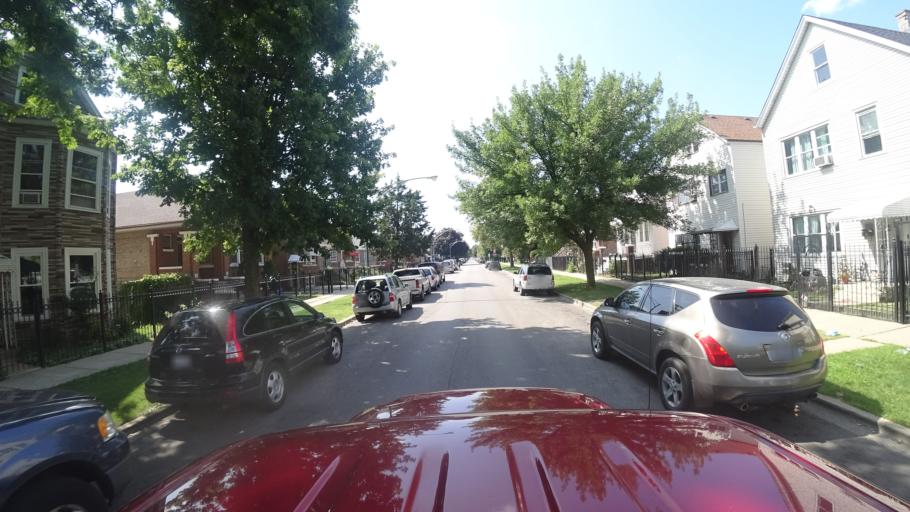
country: US
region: Illinois
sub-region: Cook County
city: Chicago
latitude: 41.8002
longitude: -87.6891
